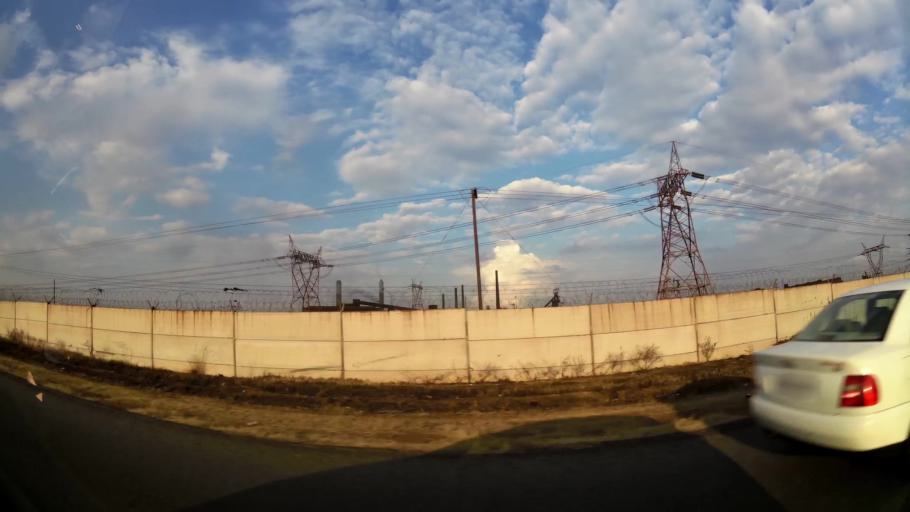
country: ZA
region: Gauteng
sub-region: Sedibeng District Municipality
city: Vanderbijlpark
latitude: -26.6557
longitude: 27.8022
